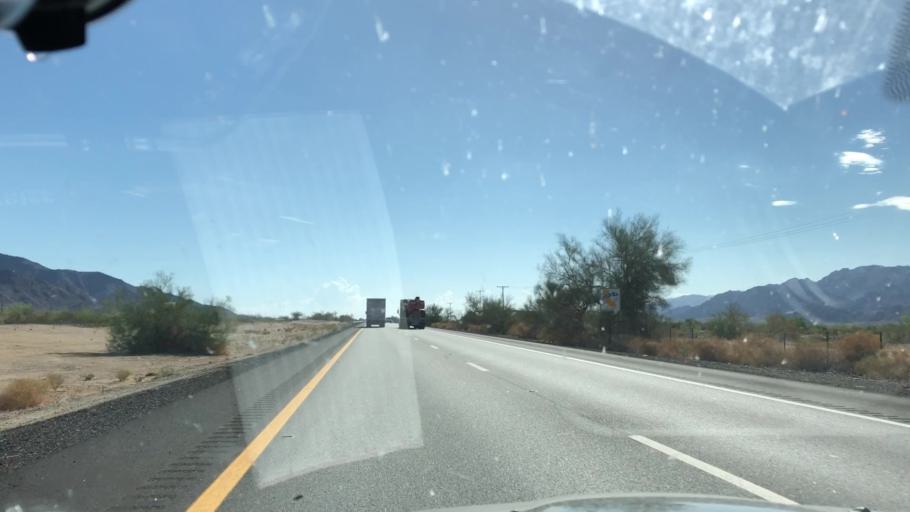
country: US
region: California
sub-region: Imperial County
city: Niland
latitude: 33.7056
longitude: -115.4373
